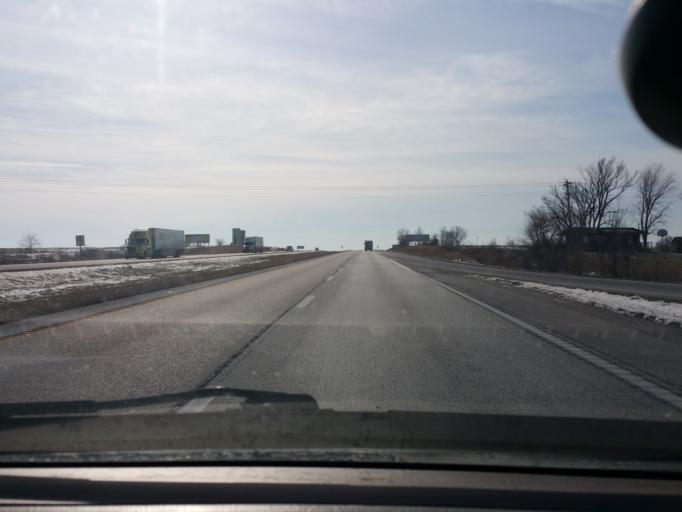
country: US
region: Missouri
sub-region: Clinton County
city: Lathrop
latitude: 39.5509
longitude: -94.2704
